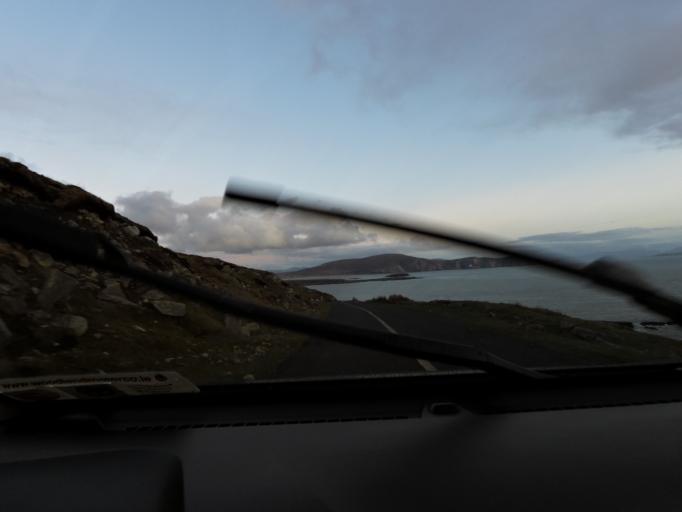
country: IE
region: Connaught
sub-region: Maigh Eo
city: Belmullet
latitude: 53.9695
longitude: -10.1615
